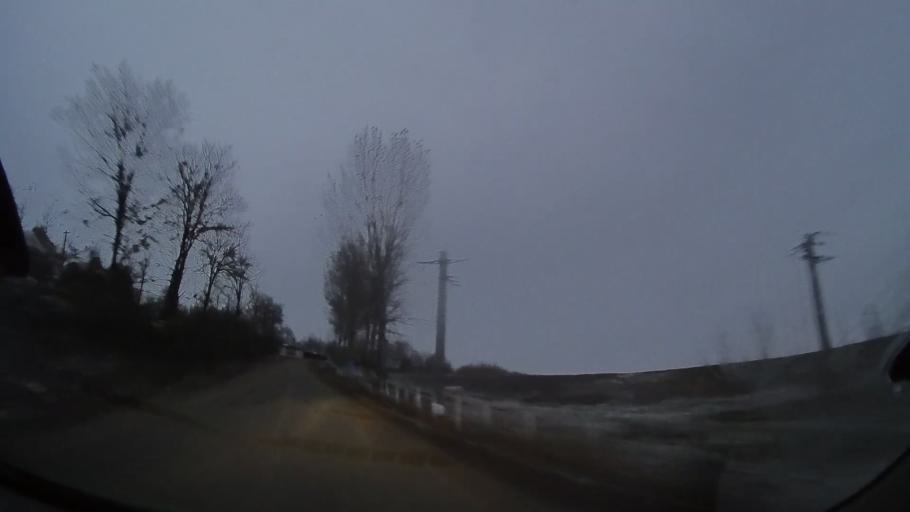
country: RO
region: Vaslui
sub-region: Comuna Vutcani
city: Vutcani
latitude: 46.4169
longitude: 27.9978
